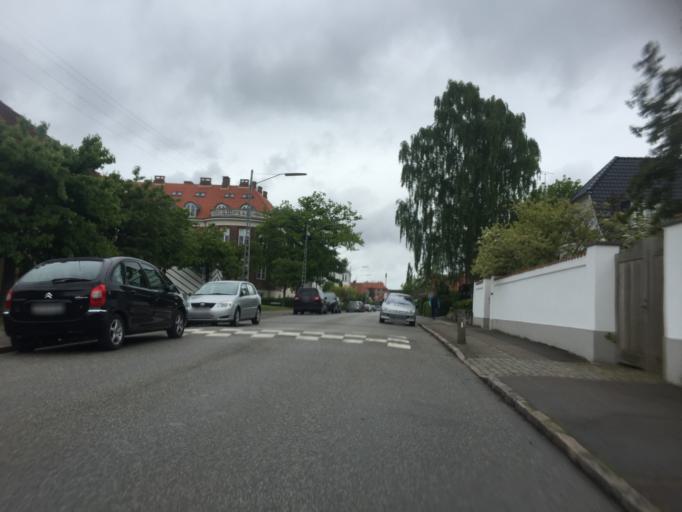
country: DK
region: Capital Region
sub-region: Frederiksberg Kommune
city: Frederiksberg
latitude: 55.6913
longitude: 12.5254
